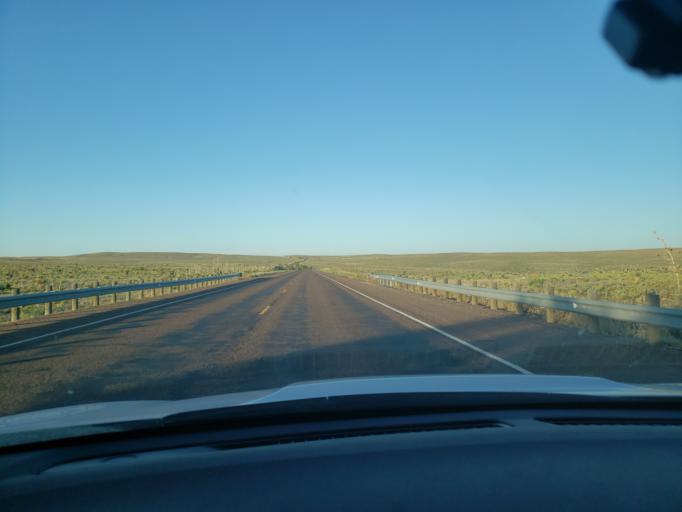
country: US
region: Texas
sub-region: El Paso County
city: Homestead Meadows South
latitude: 31.8286
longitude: -105.8729
